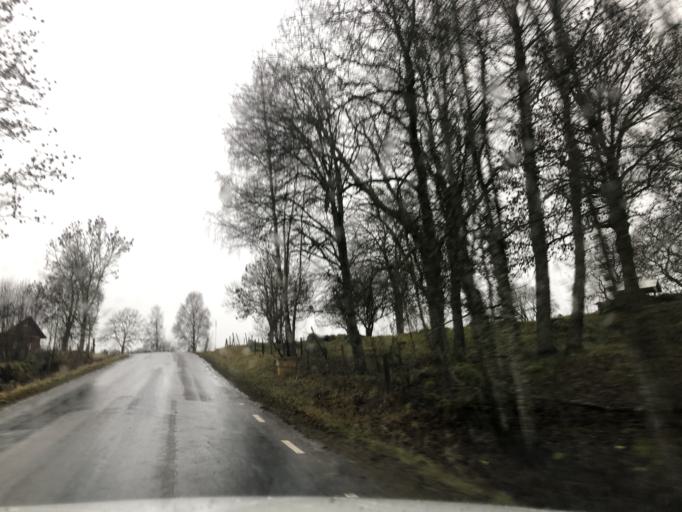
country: SE
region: Vaestra Goetaland
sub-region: Ulricehamns Kommun
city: Ulricehamn
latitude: 57.8490
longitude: 13.5426
